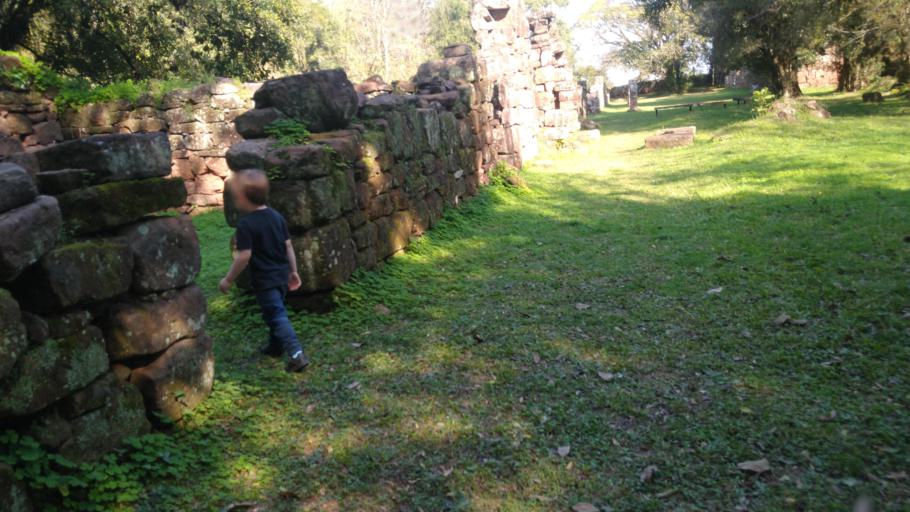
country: AR
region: Misiones
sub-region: Departamento de San Ignacio
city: San Ignacio
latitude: -27.2542
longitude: -55.5303
